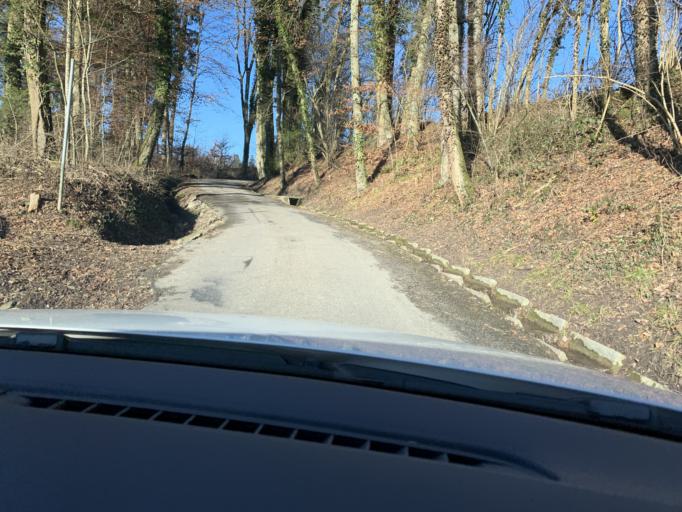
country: CH
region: Zurich
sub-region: Bezirk Dielsdorf
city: Sonnhalde
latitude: 47.4562
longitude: 8.4589
